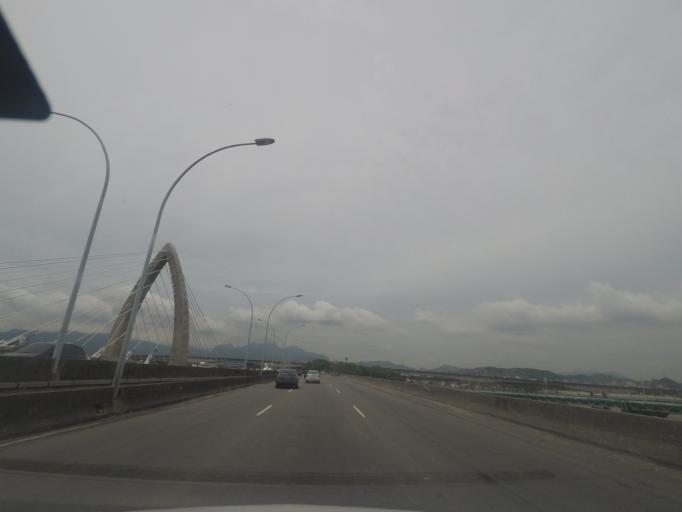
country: BR
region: Rio de Janeiro
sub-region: Rio De Janeiro
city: Rio de Janeiro
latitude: -22.8356
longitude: -43.2408
